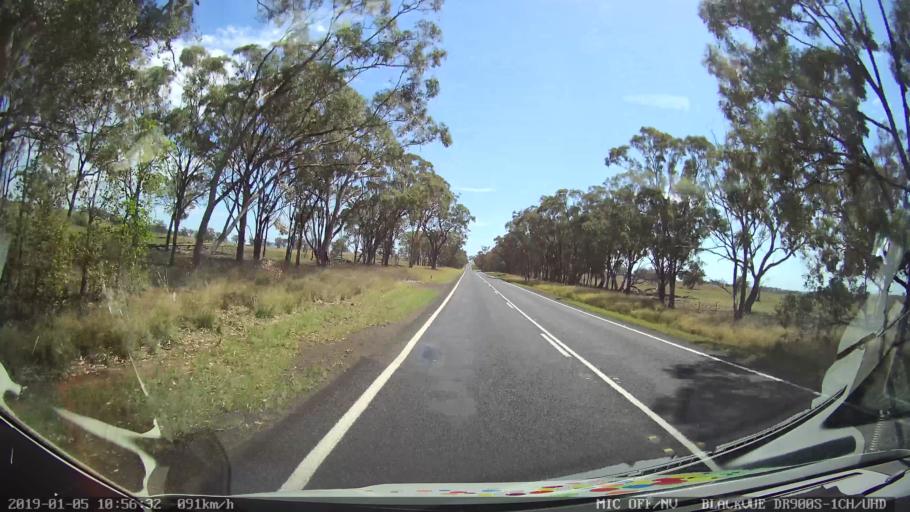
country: AU
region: New South Wales
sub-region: Warrumbungle Shire
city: Coonabarabran
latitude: -31.4404
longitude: 149.1593
